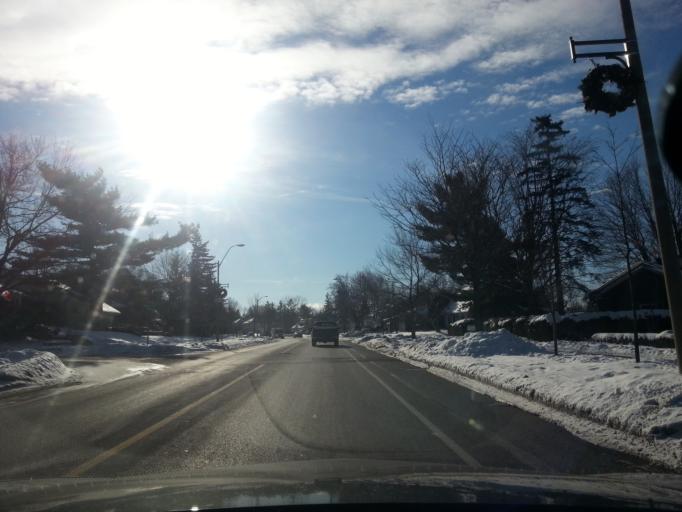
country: CA
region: Ontario
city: Ottawa
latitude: 45.3963
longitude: -75.6623
